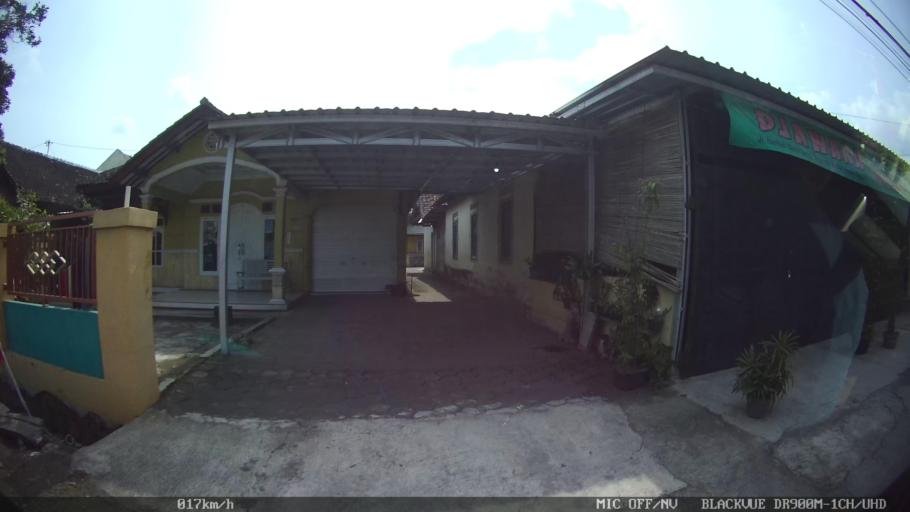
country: ID
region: Daerah Istimewa Yogyakarta
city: Depok
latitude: -7.7913
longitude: 110.4465
